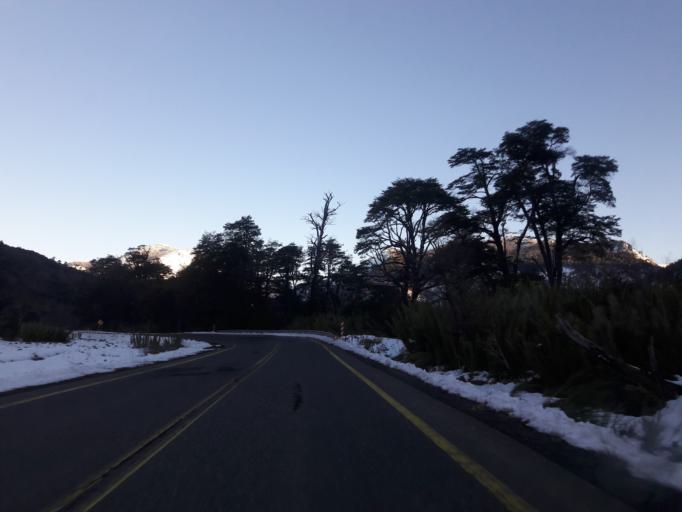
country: CL
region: Araucania
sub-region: Provincia de Cautin
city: Vilcun
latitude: -38.4938
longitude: -71.5221
